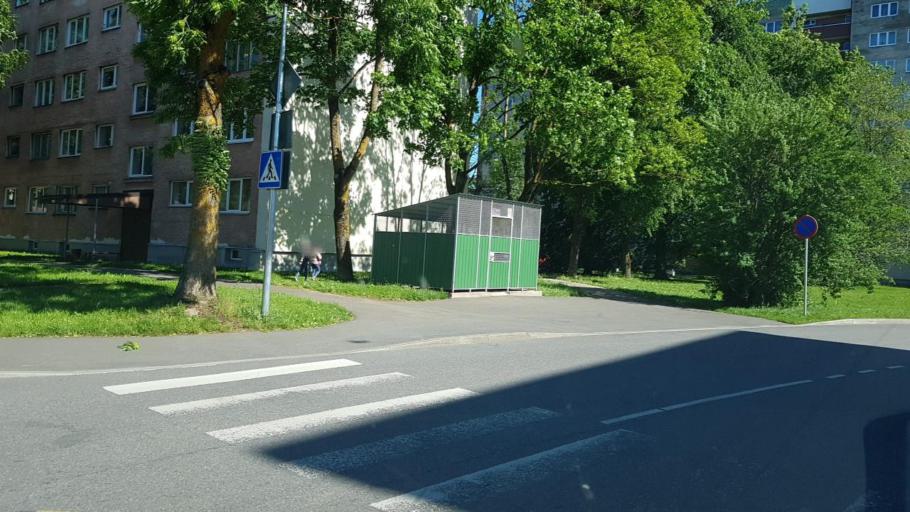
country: EE
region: Ida-Virumaa
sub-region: Narva linn
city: Narva
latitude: 59.3694
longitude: 28.1797
